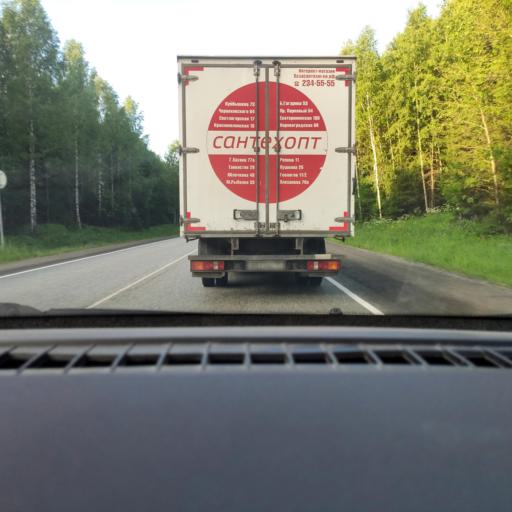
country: RU
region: Perm
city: Pavlovskiy
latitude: 57.9059
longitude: 54.9551
